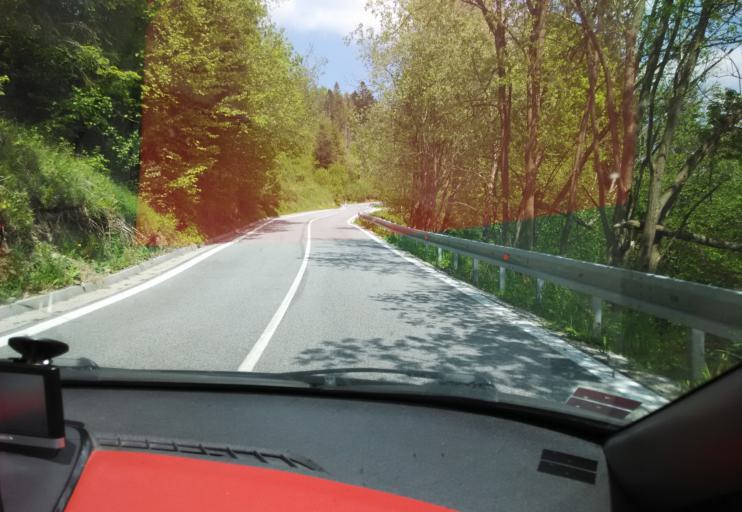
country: SK
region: Kosicky
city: Dobsina
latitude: 48.8459
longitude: 20.4419
